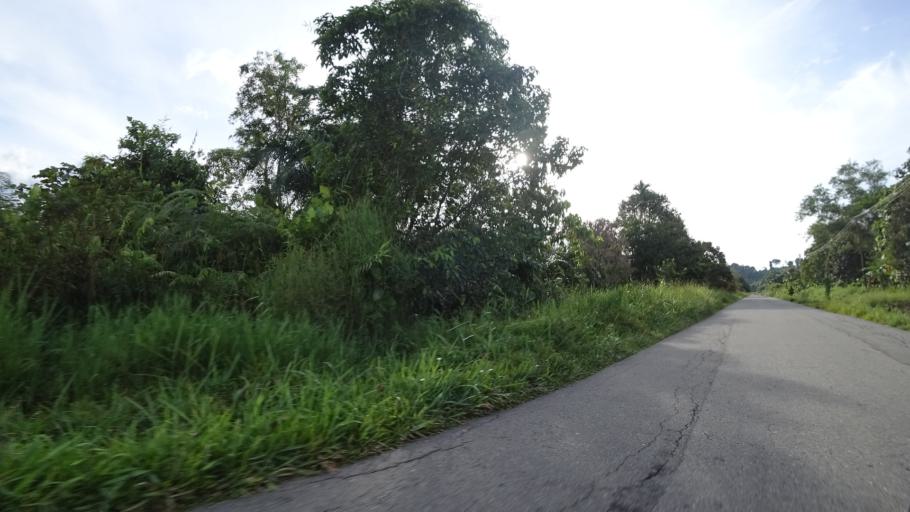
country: BN
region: Tutong
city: Tutong
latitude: 4.8169
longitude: 114.8217
